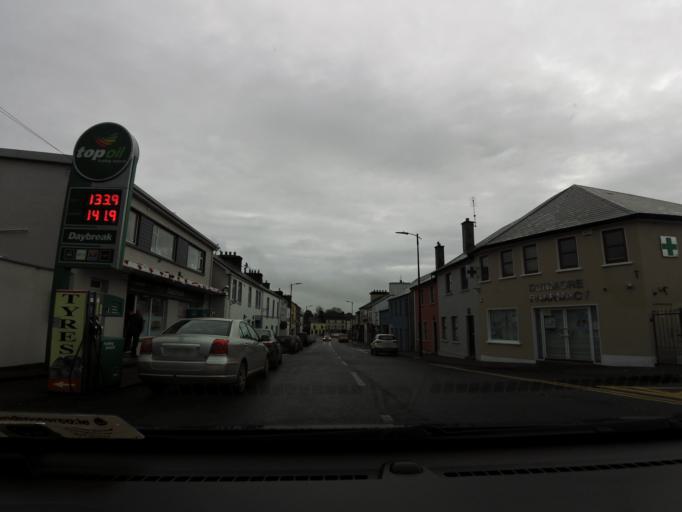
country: IE
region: Connaught
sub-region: County Galway
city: Tuam
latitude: 53.6174
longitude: -8.7451
